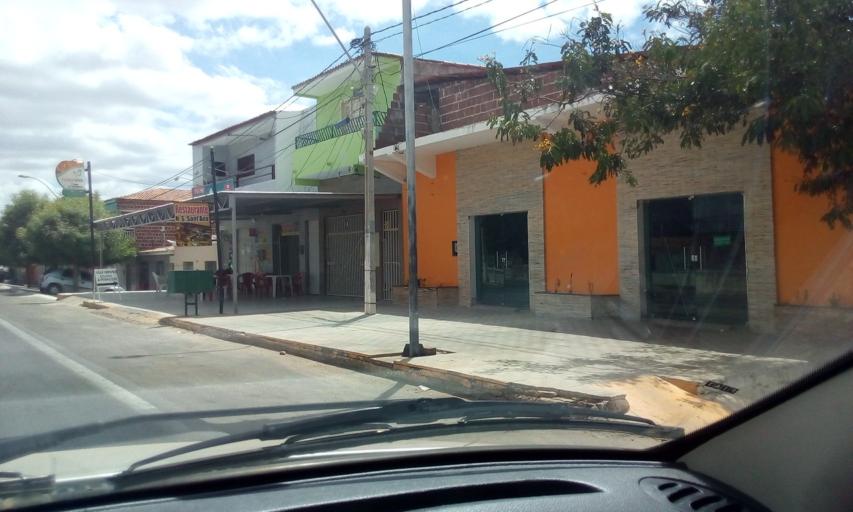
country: BR
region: Rio Grande do Norte
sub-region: Currais Novos
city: Currais Novos
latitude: -6.2580
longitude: -36.5090
